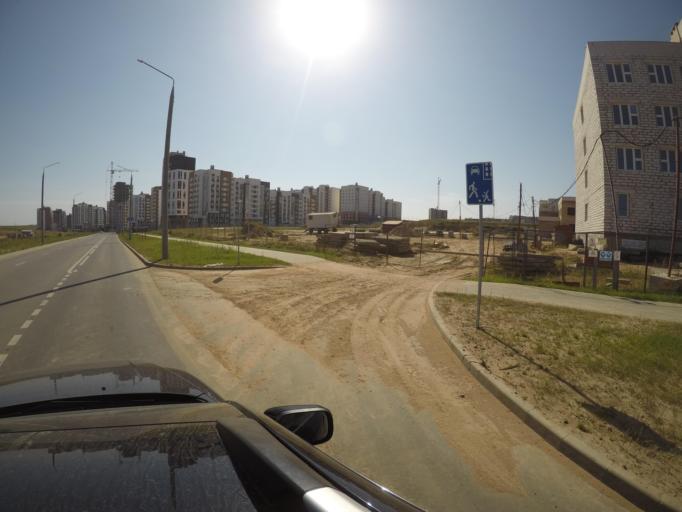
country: BY
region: Grodnenskaya
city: Hrodna
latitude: 53.7229
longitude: 23.8774
